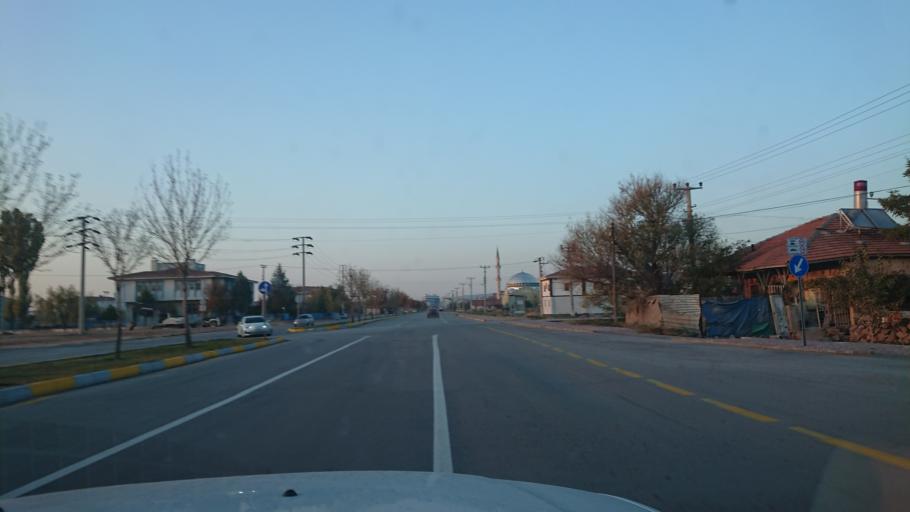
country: TR
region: Aksaray
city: Aksaray
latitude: 38.3447
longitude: 34.0454
